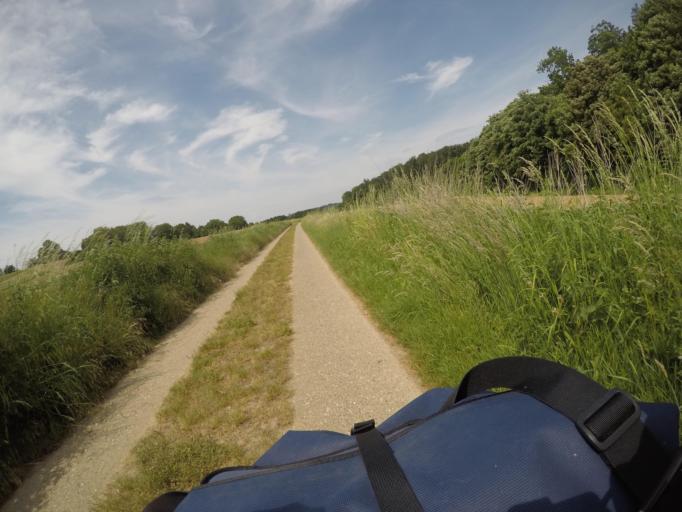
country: DE
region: Baden-Wuerttemberg
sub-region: Karlsruhe Region
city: Weingarten
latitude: 48.9744
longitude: 8.4982
